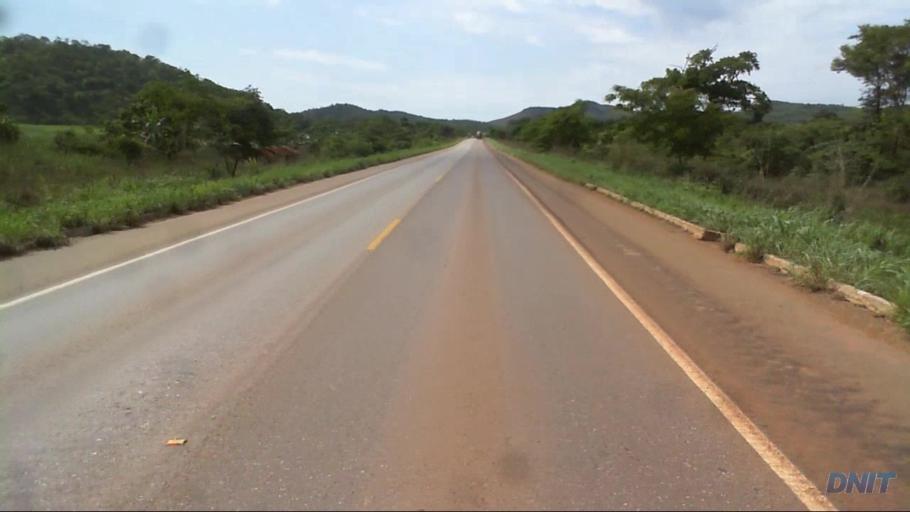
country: BR
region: Goias
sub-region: Barro Alto
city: Barro Alto
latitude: -15.1221
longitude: -48.8371
